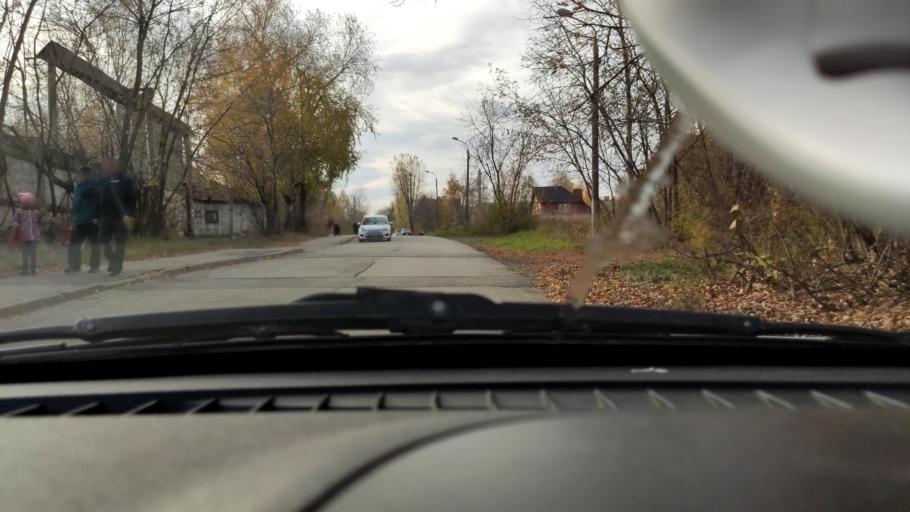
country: RU
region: Perm
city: Polazna
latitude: 58.1234
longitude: 56.3825
